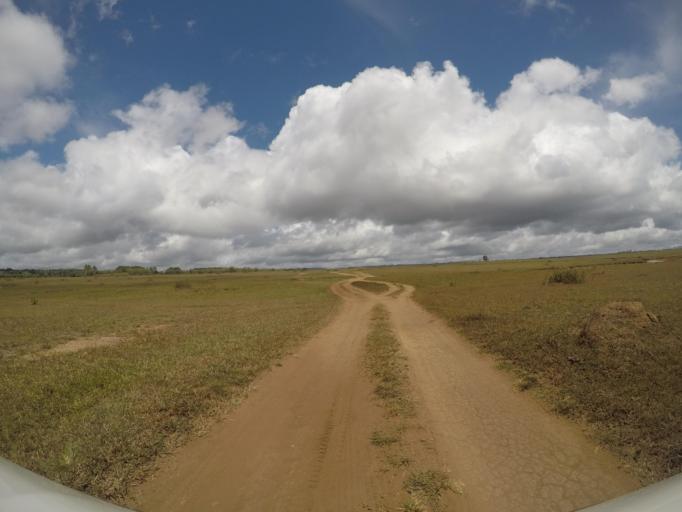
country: TL
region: Lautem
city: Lospalos
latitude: -8.4642
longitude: 126.9850
